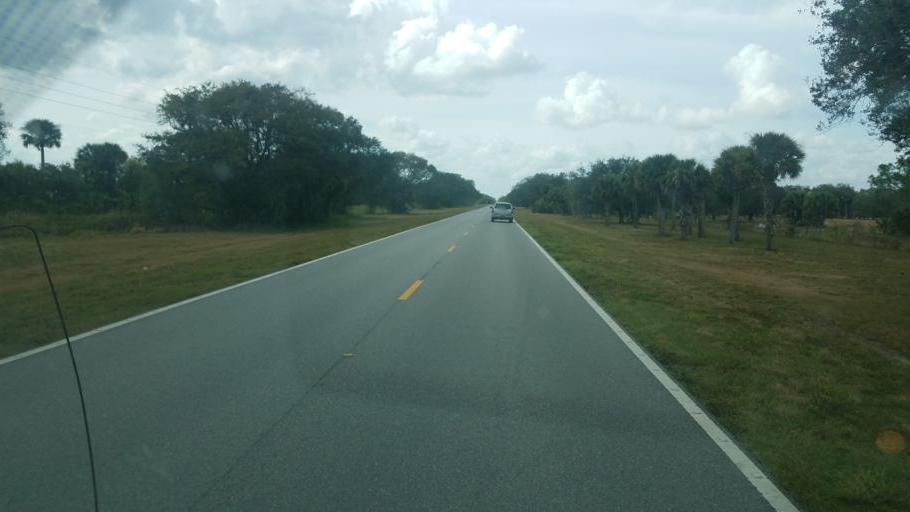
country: US
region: Florida
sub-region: Okeechobee County
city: Cypress Quarters
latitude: 27.4500
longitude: -80.7000
